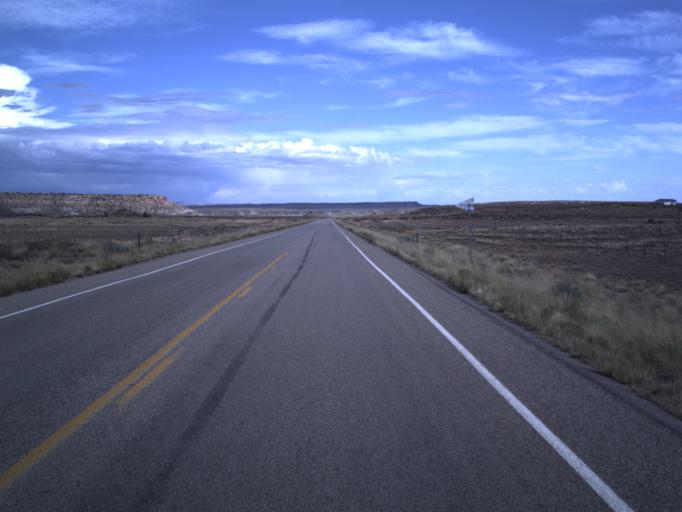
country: US
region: Colorado
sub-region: Montezuma County
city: Towaoc
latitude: 37.1705
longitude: -109.0887
